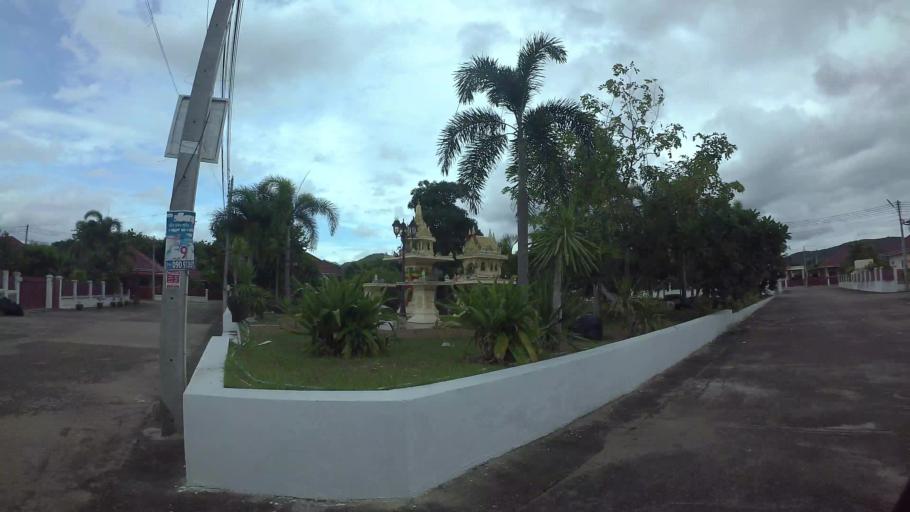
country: TH
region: Chon Buri
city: Sattahip
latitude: 12.7237
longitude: 100.9061
